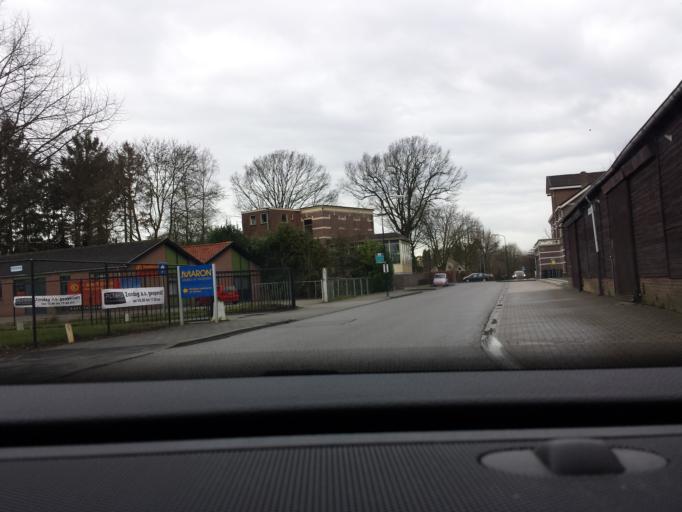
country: NL
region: Gelderland
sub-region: Oude IJsselstreek
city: Gendringen
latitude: 51.9220
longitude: 6.3647
